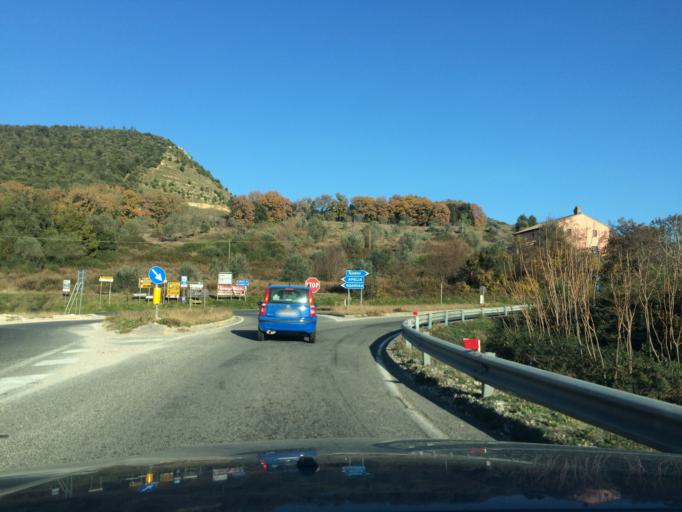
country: IT
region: Umbria
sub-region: Provincia di Terni
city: Fornole
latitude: 42.5382
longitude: 12.4781
